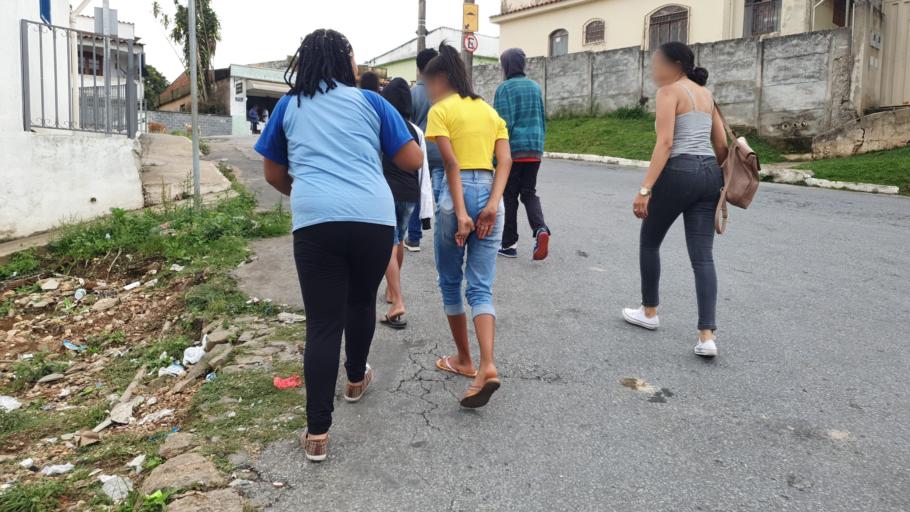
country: BR
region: Minas Gerais
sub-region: Sao Joao Del Rei
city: Sao Joao del Rei
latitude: -21.1272
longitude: -44.2640
